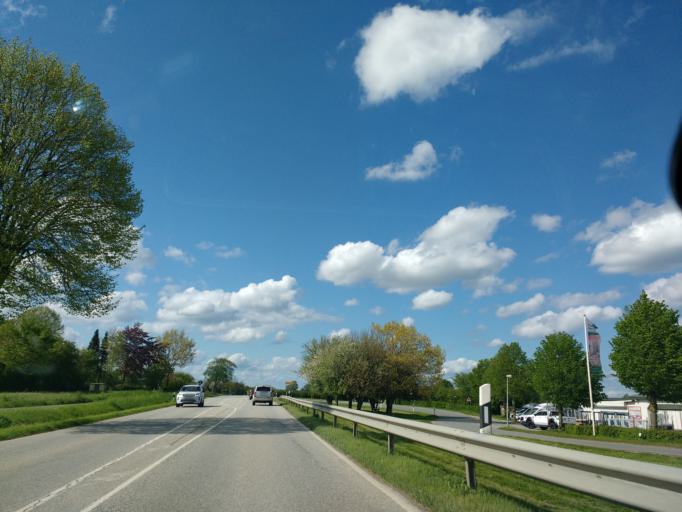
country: DE
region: Schleswig-Holstein
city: Rabel
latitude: 54.6958
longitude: 9.9443
